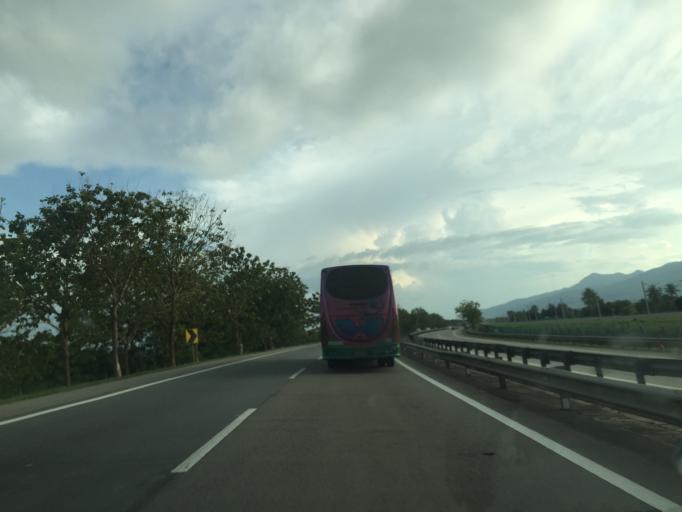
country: MY
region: Kedah
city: Gurun
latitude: 5.8925
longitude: 100.4772
